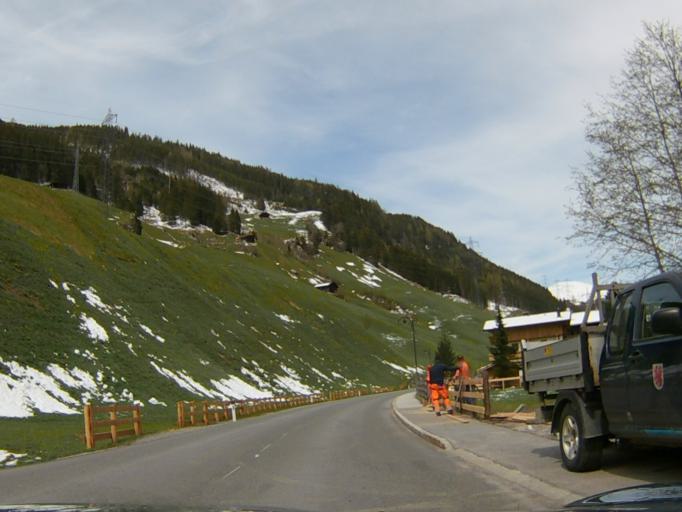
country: AT
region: Tyrol
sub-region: Politischer Bezirk Schwaz
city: Gerlos
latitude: 47.2128
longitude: 12.0061
